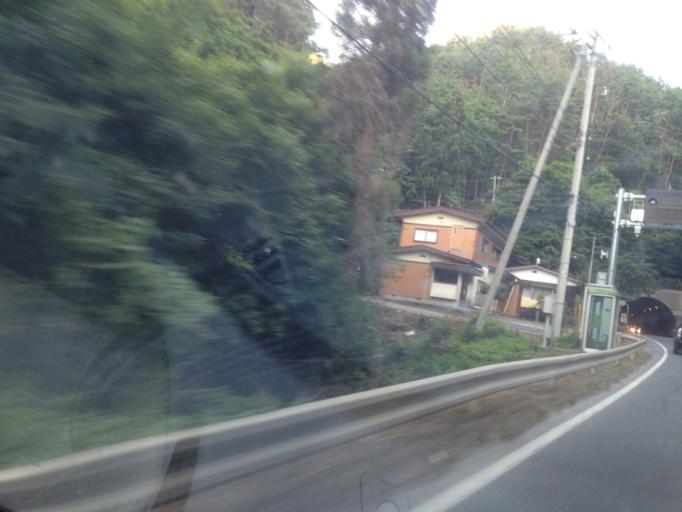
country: JP
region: Iwate
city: Otsuchi
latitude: 39.3514
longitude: 141.8932
